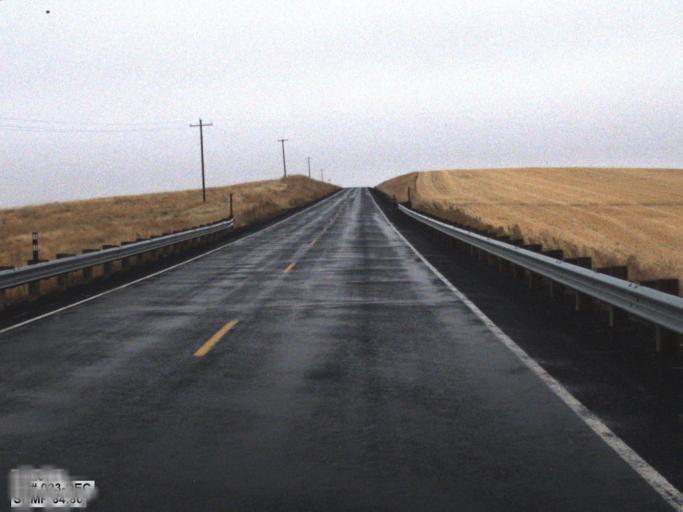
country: US
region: Washington
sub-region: Lincoln County
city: Davenport
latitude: 47.4783
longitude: -118.2392
